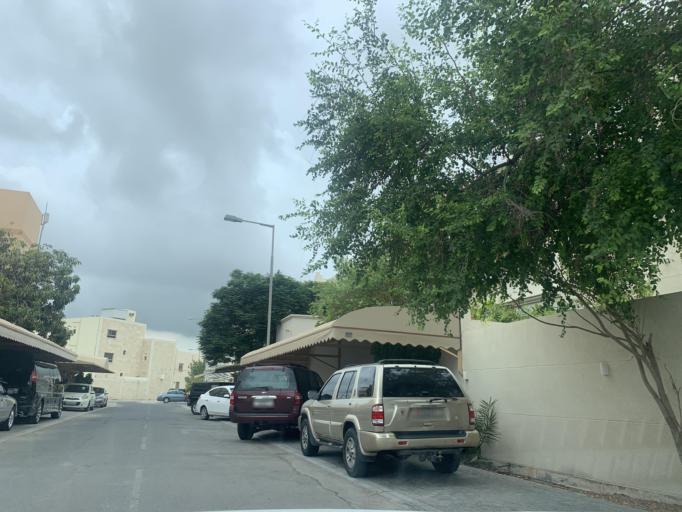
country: BH
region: Muharraq
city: Al Hadd
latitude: 26.2768
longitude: 50.6457
